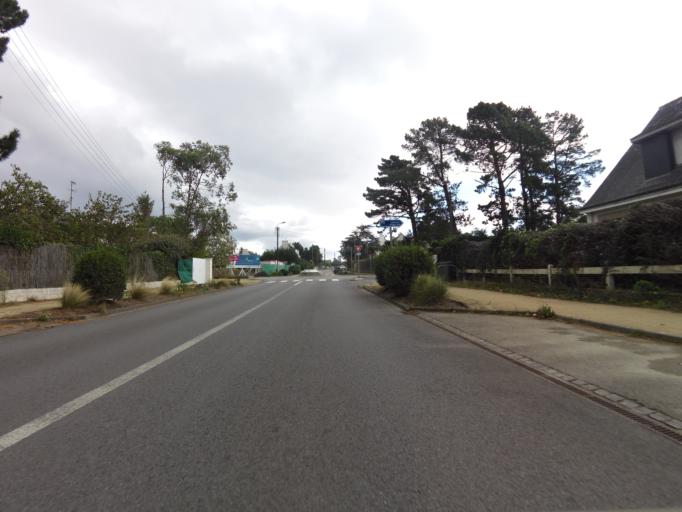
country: FR
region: Brittany
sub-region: Departement du Morbihan
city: Carnac
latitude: 47.5760
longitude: -3.0583
